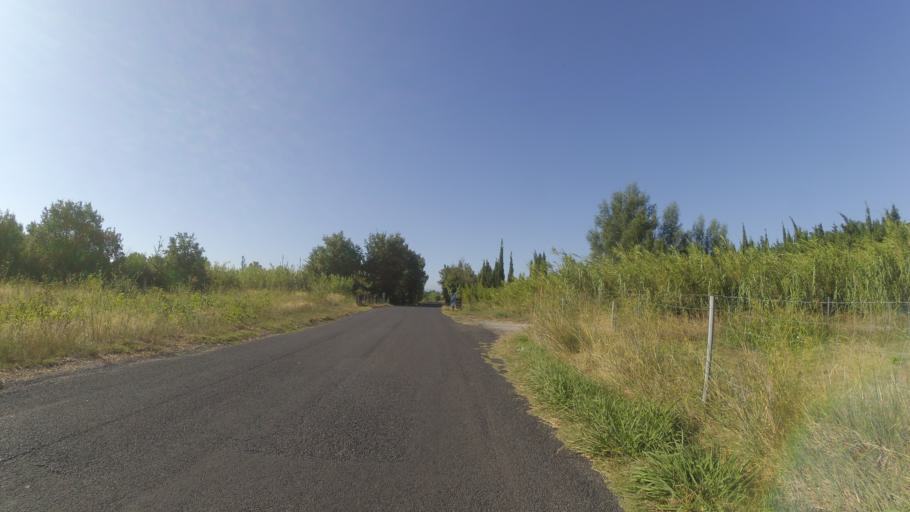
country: FR
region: Languedoc-Roussillon
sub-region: Departement des Pyrenees-Orientales
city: Villeneuve-la-Riviere
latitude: 42.7019
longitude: 2.7993
